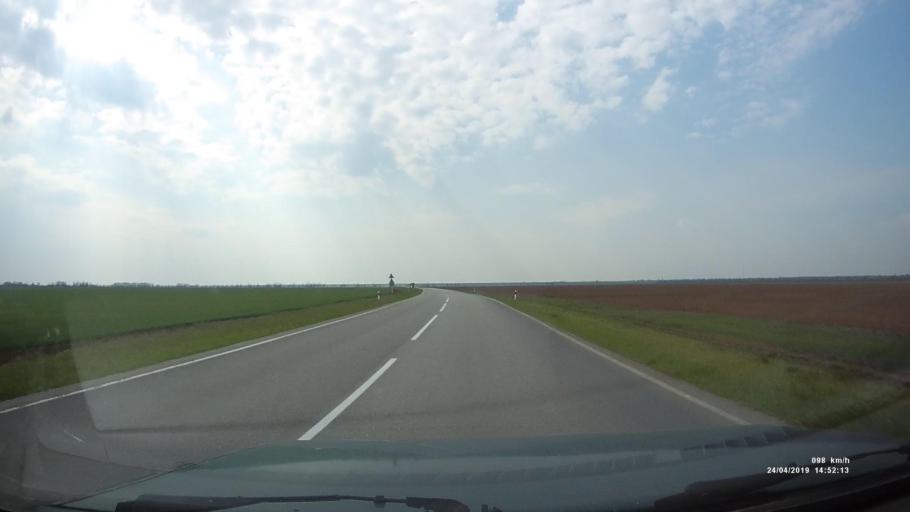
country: RU
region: Rostov
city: Remontnoye
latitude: 46.5298
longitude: 43.6855
